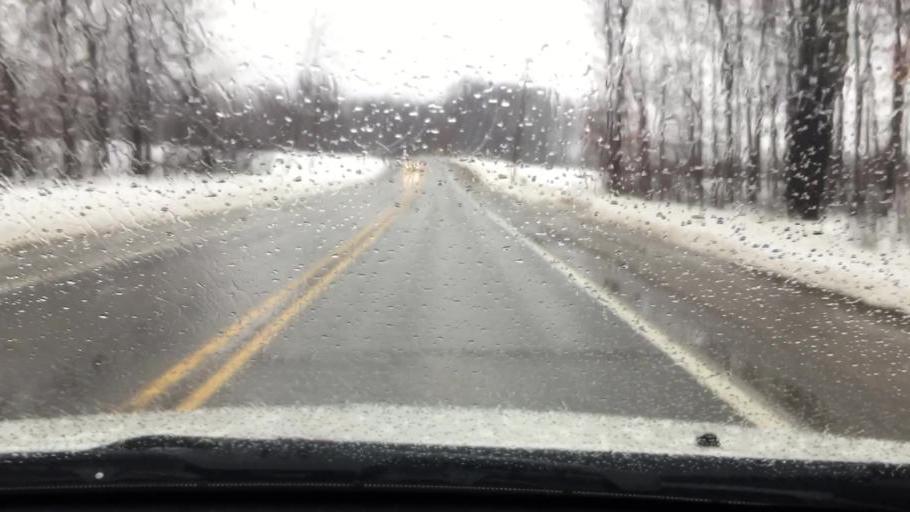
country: US
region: Michigan
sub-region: Charlevoix County
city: East Jordan
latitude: 45.2064
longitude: -85.1656
